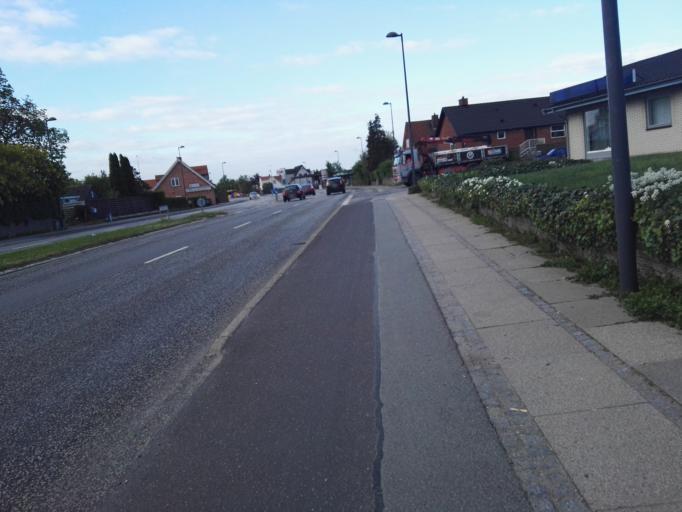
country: DK
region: Capital Region
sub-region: Ballerup Kommune
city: Ballerup
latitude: 55.7261
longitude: 12.3567
